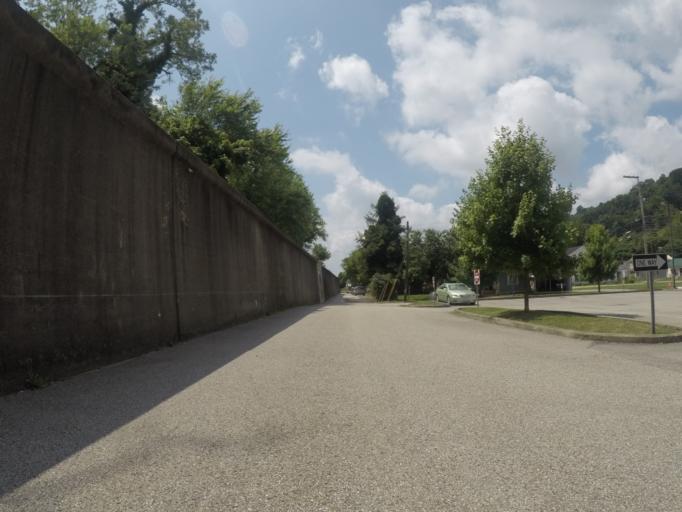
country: US
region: Kentucky
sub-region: Boyd County
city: Catlettsburg
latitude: 38.4148
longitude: -82.5973
